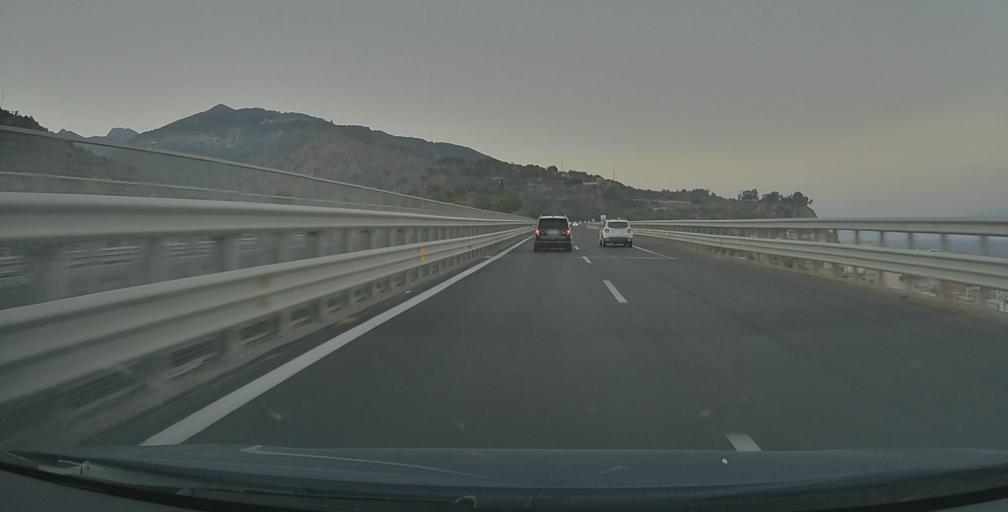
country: IT
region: Sicily
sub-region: Messina
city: Ali Terme
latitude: 38.0047
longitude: 15.4211
